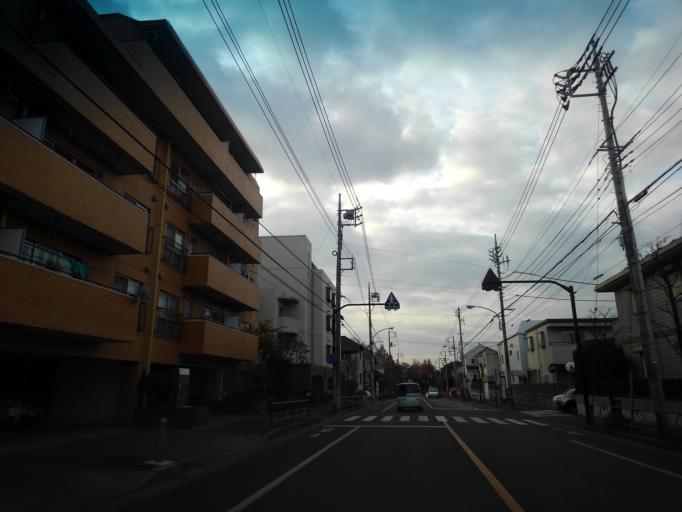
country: JP
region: Tokyo
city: Tanashicho
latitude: 35.7197
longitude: 139.5091
